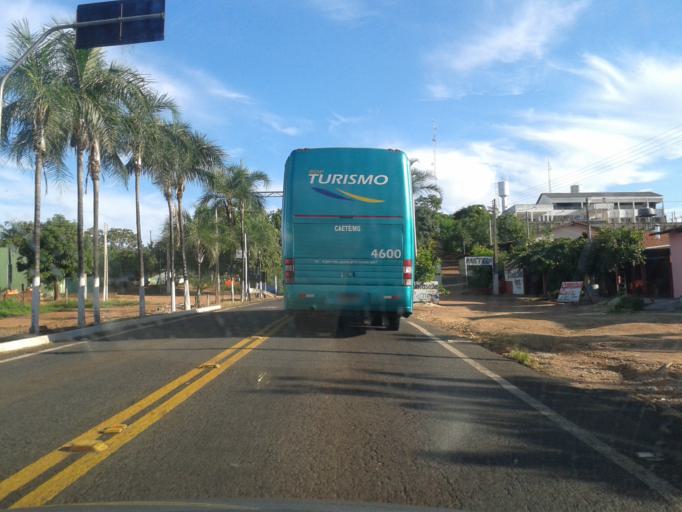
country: BR
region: Minas Gerais
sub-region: Tupaciguara
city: Tupaciguara
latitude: -18.3127
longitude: -48.5620
